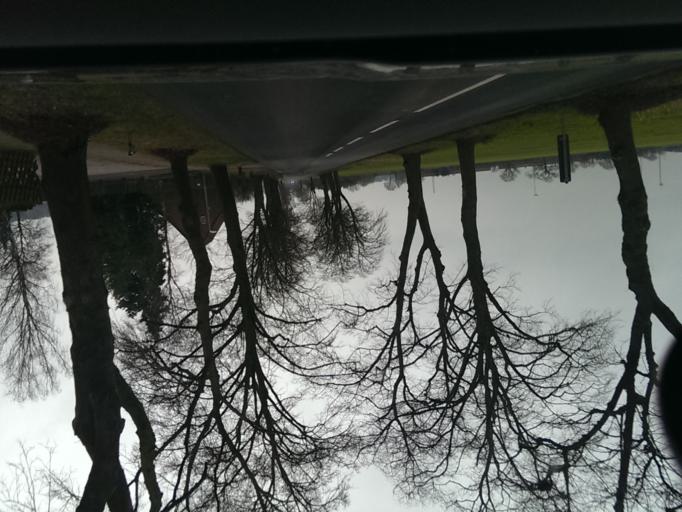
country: DE
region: Lower Saxony
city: Elze
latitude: 52.5788
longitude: 9.7426
